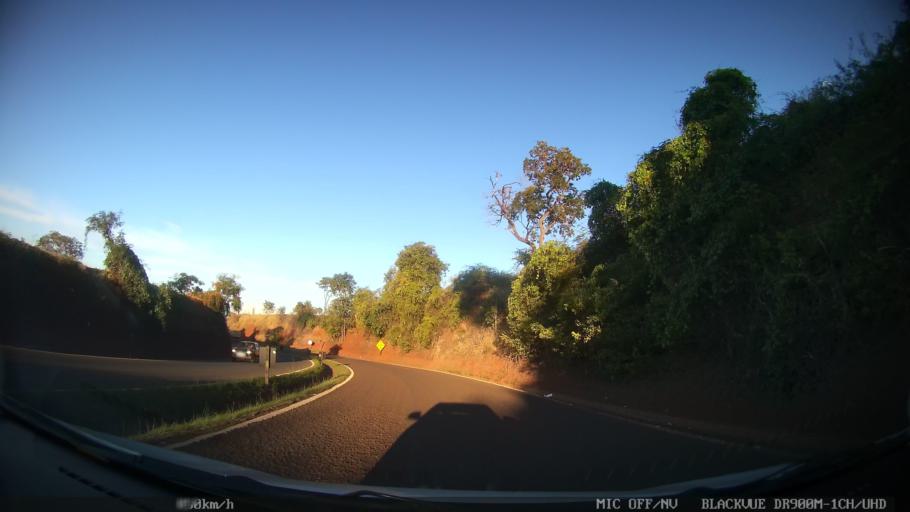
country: BR
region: Sao Paulo
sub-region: Araraquara
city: Araraquara
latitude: -21.7895
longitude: -48.2193
